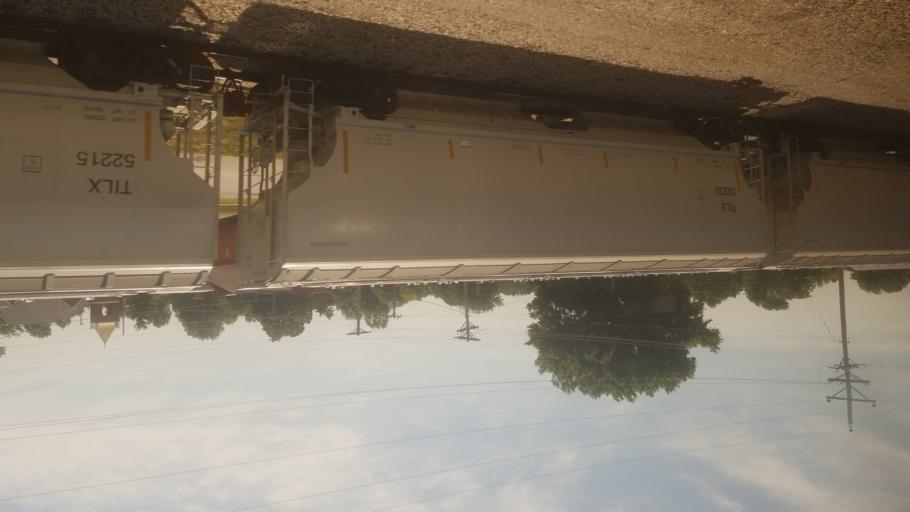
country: US
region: Missouri
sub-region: Carroll County
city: Carrollton
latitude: 39.3037
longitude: -93.6763
